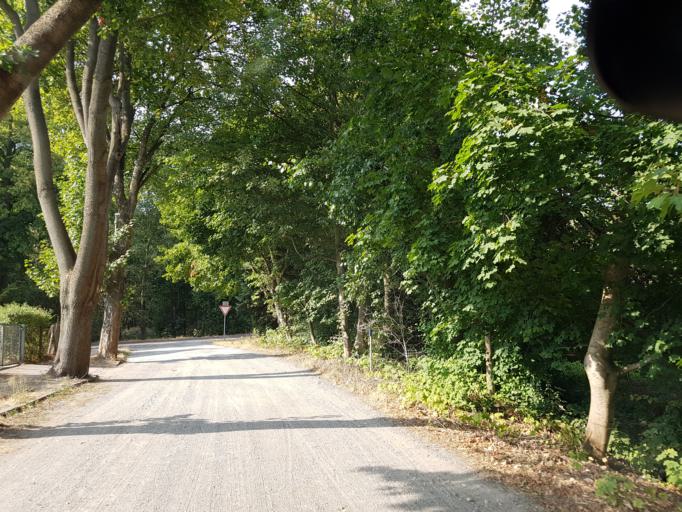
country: DE
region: Saxony-Anhalt
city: Nudersdorf
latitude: 51.8797
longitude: 12.5547
